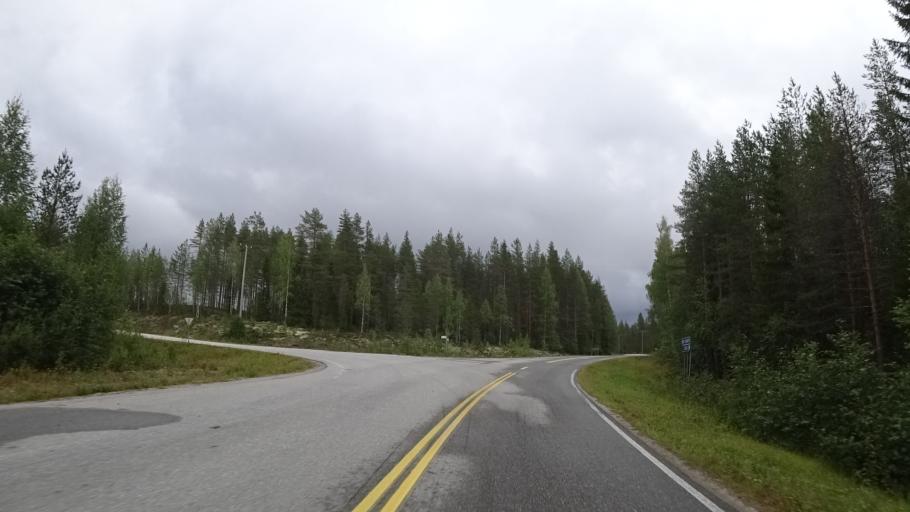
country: FI
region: North Karelia
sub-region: Joensuu
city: Ilomantsi
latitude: 63.2537
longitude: 30.7409
